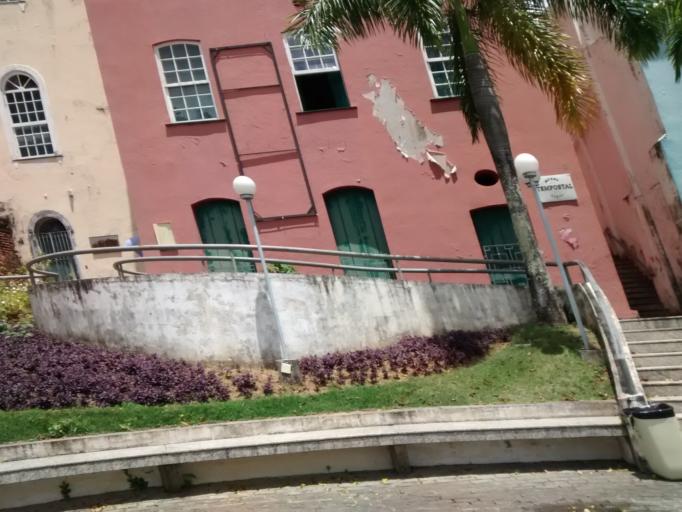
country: BR
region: Bahia
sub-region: Salvador
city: Salvador
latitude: -12.9729
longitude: -38.5081
